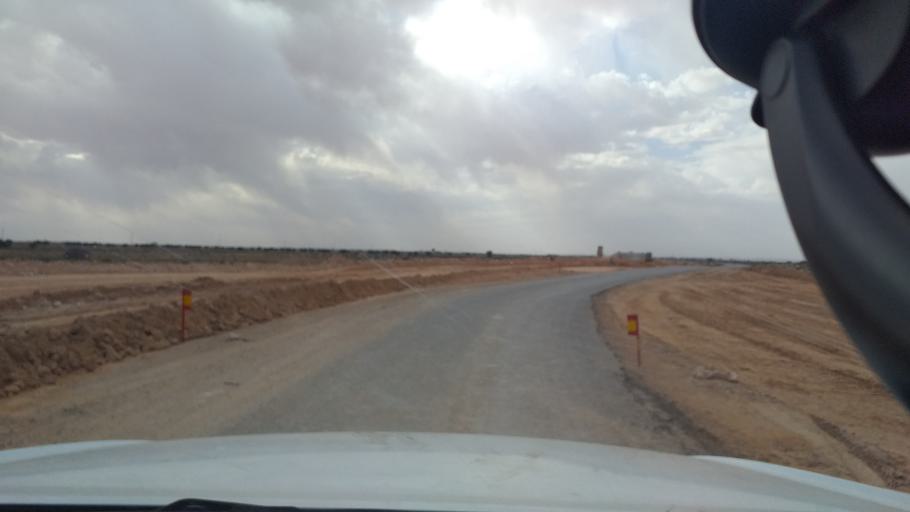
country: TN
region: Madanin
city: Medenine
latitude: 33.3063
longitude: 10.6130
